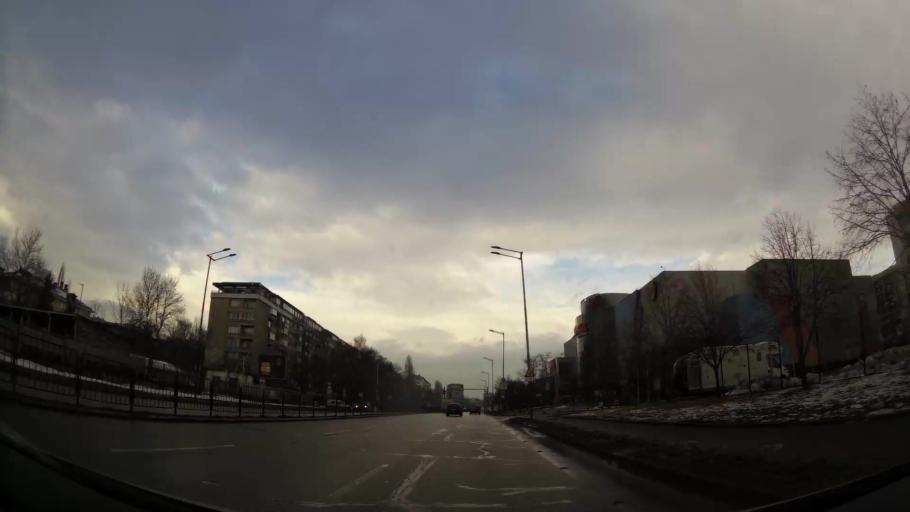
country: BG
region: Sofia-Capital
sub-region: Stolichna Obshtina
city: Sofia
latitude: 42.7046
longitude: 23.2911
